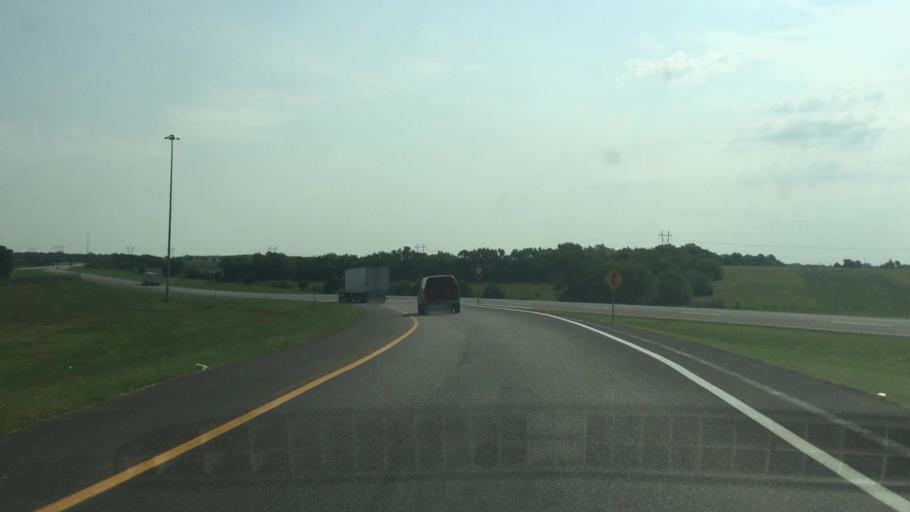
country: US
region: Kansas
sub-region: Butler County
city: Towanda
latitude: 37.7664
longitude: -96.9795
